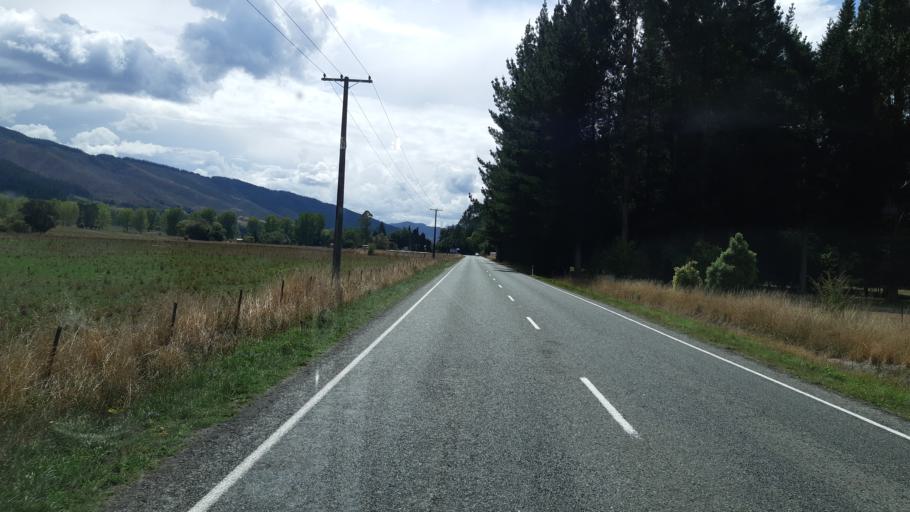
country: NZ
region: Tasman
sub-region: Tasman District
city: Wakefield
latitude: -41.4769
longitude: 172.8036
